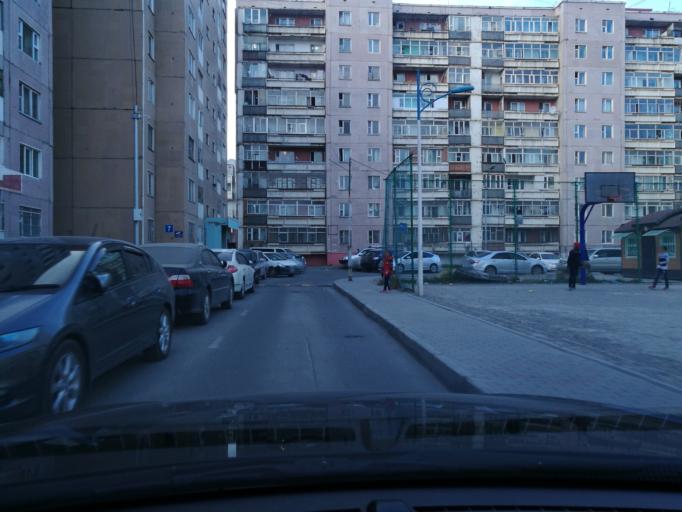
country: MN
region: Ulaanbaatar
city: Ulaanbaatar
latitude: 47.9279
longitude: 106.9281
